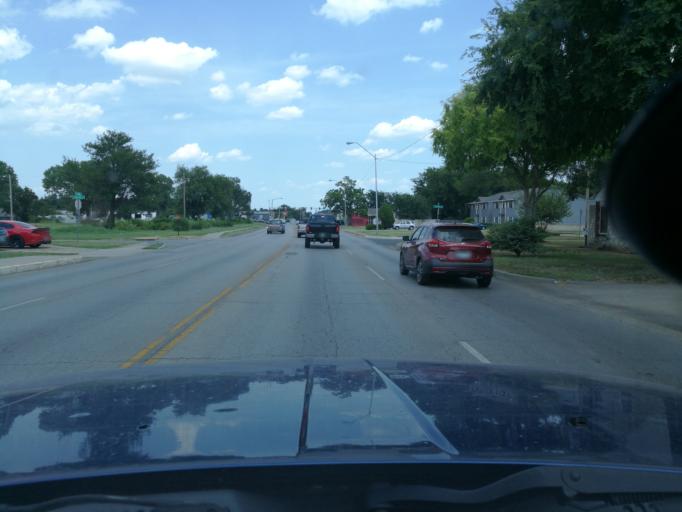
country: US
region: Oklahoma
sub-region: Oklahoma County
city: Oklahoma City
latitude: 35.4207
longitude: -97.5187
